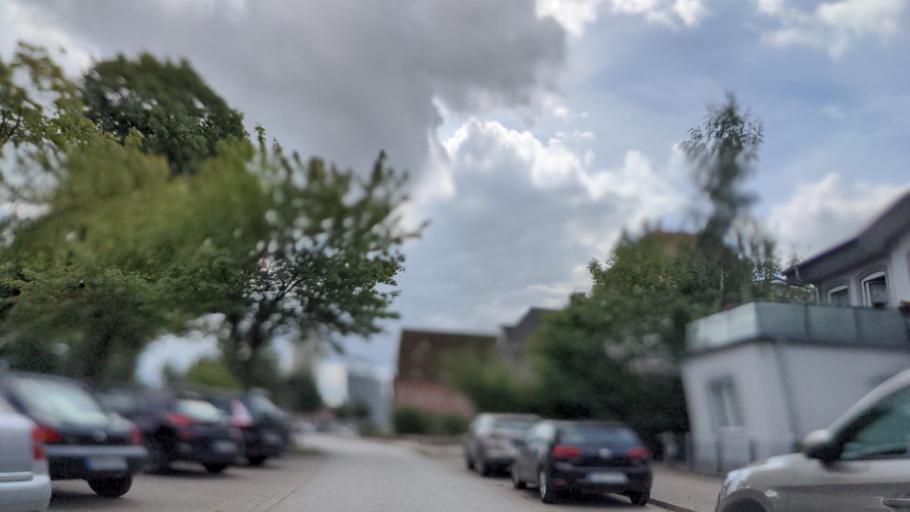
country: DE
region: Schleswig-Holstein
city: Susel
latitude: 54.0465
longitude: 10.6704
